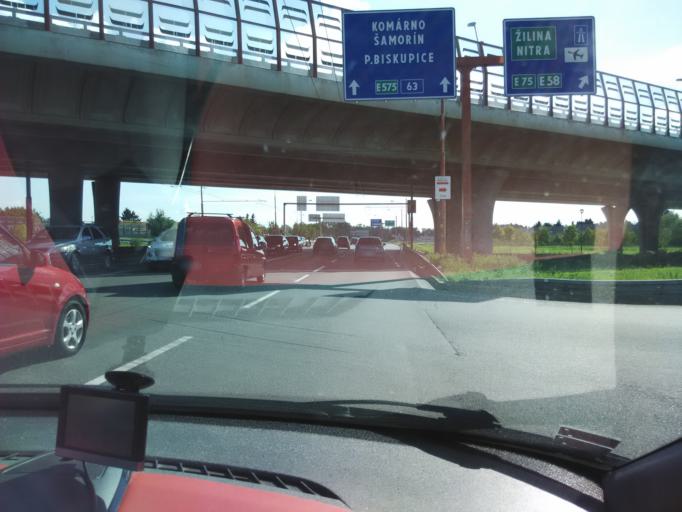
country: SK
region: Bratislavsky
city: Bratislava
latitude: 48.1499
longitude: 17.1804
